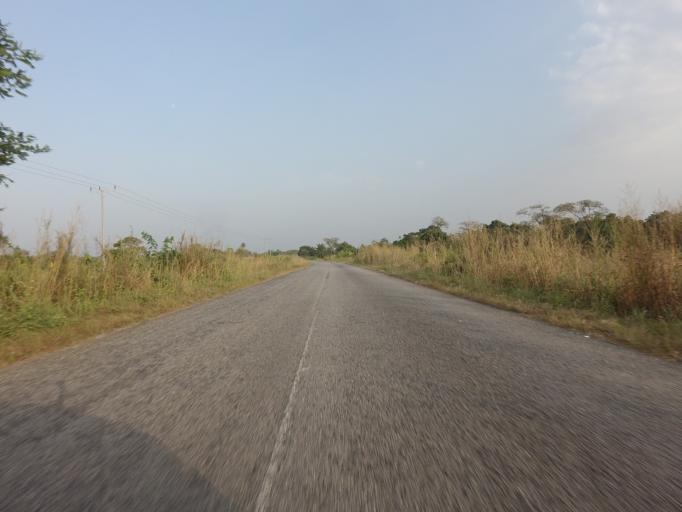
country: GH
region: Volta
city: Ho
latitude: 6.5740
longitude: 0.3424
